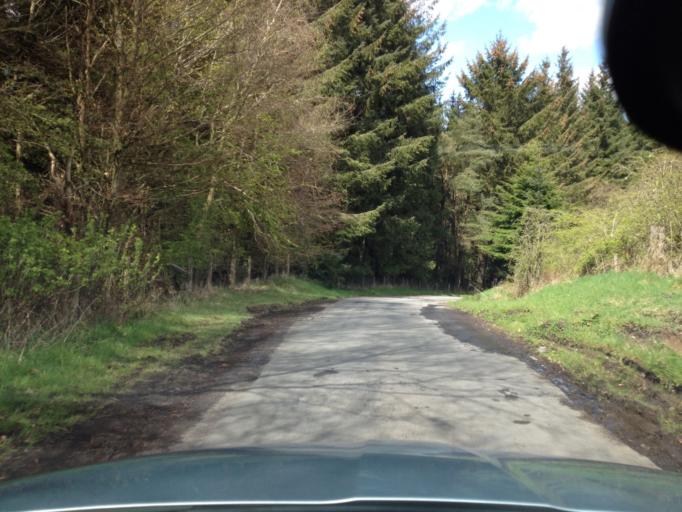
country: GB
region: Scotland
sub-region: West Lothian
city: Linlithgow
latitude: 55.9472
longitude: -3.5890
